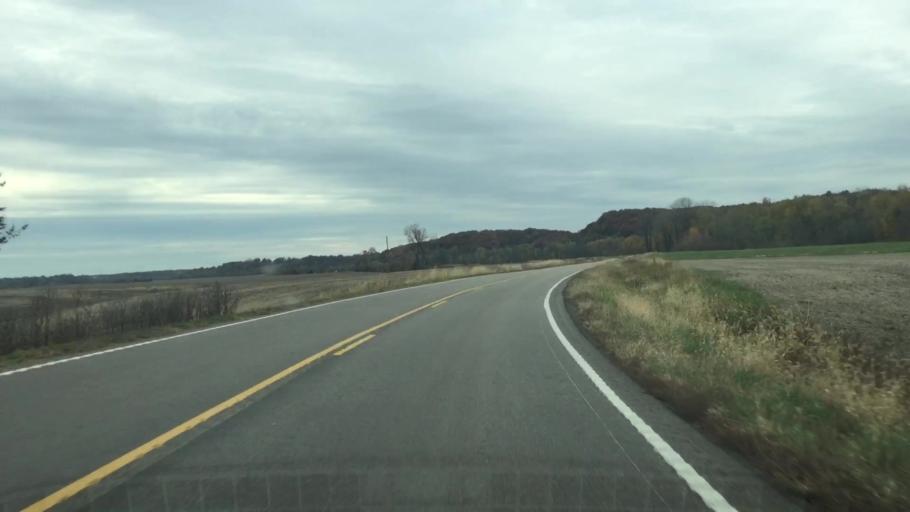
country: US
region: Missouri
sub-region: Callaway County
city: Fulton
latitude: 38.7048
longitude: -91.7753
